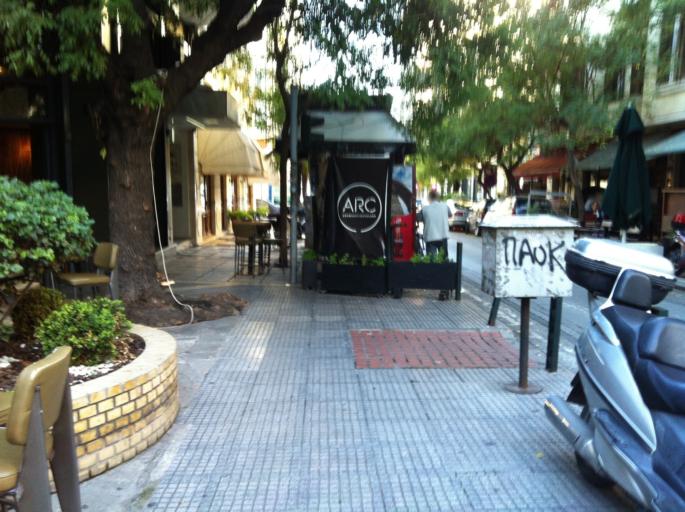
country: GR
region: Central Macedonia
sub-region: Nomos Thessalonikis
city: Thessaloniki
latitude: 40.6336
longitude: 22.9398
